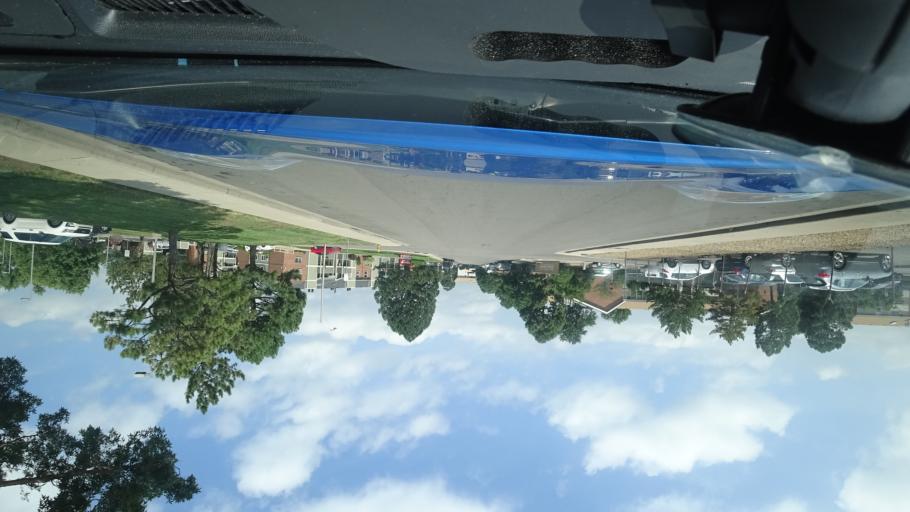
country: US
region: Colorado
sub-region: Adams County
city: Aurora
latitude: 39.7074
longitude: -104.8678
